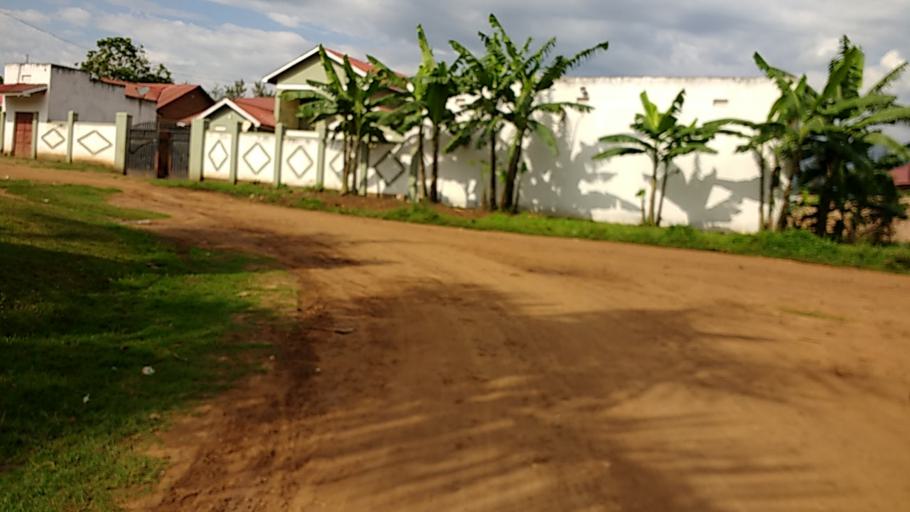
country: UG
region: Eastern Region
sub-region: Mbale District
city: Mbale
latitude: 1.0666
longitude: 34.1696
